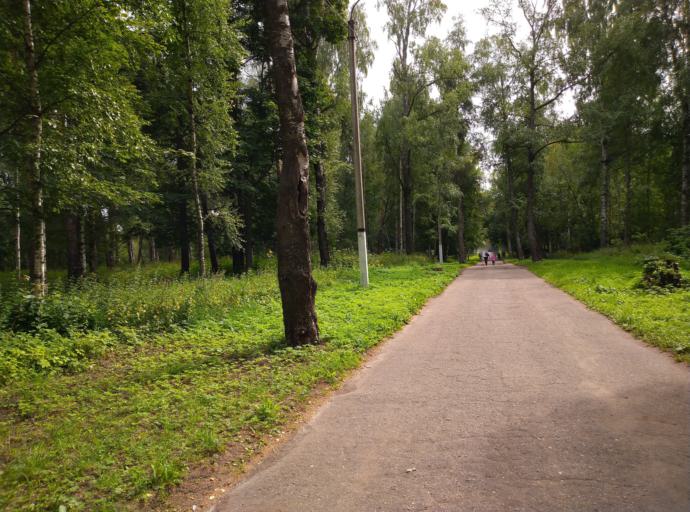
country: RU
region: Kostroma
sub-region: Kostromskoy Rayon
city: Kostroma
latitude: 57.7813
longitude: 40.9604
